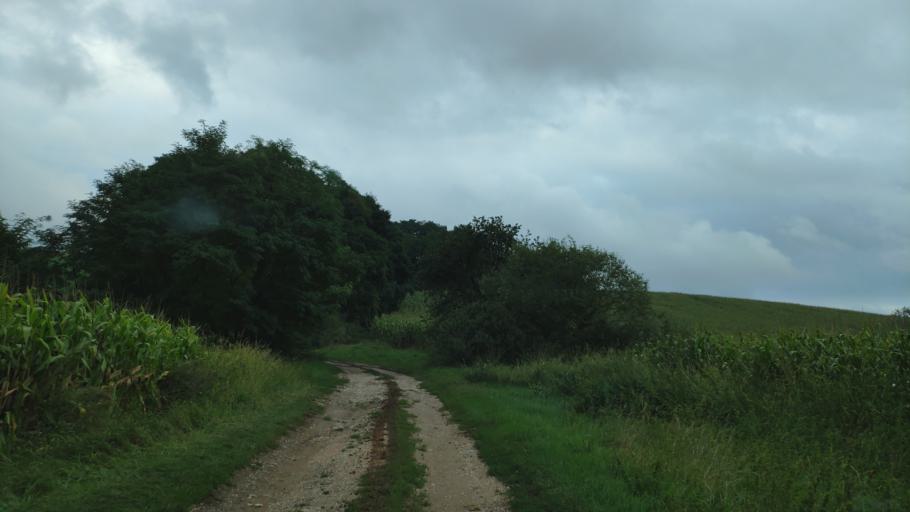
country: SK
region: Kosicky
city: Moldava nad Bodvou
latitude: 48.5796
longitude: 20.9017
